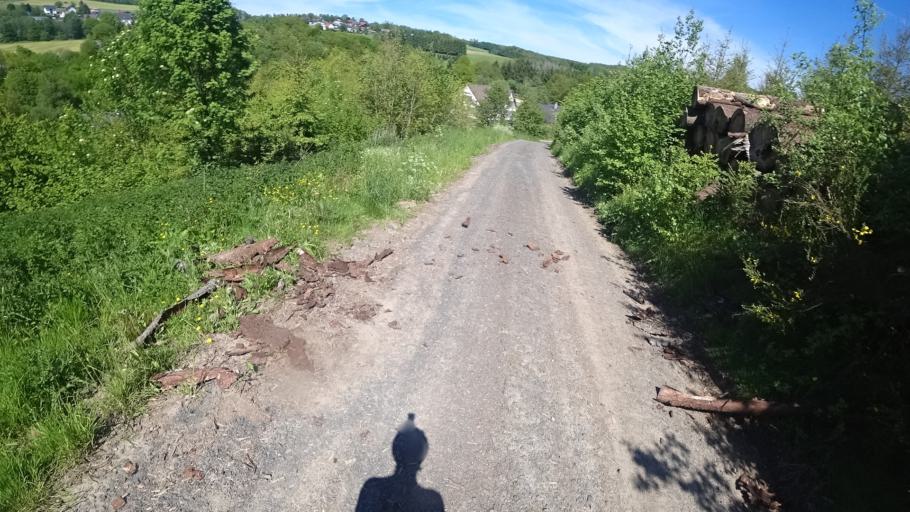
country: DE
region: Rheinland-Pfalz
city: Steineroth
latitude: 50.7446
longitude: 7.8531
